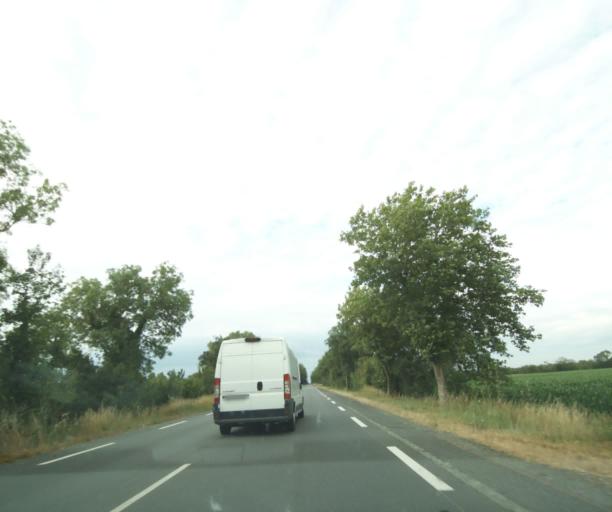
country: FR
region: Poitou-Charentes
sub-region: Departement de la Charente-Maritime
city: Andilly
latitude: 46.2718
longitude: -1.0029
